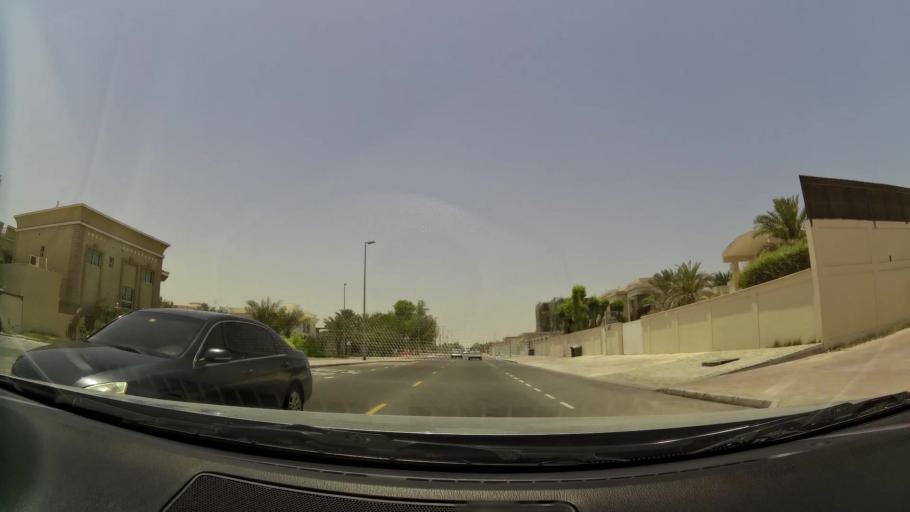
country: AE
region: Dubai
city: Dubai
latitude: 25.1813
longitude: 55.2318
